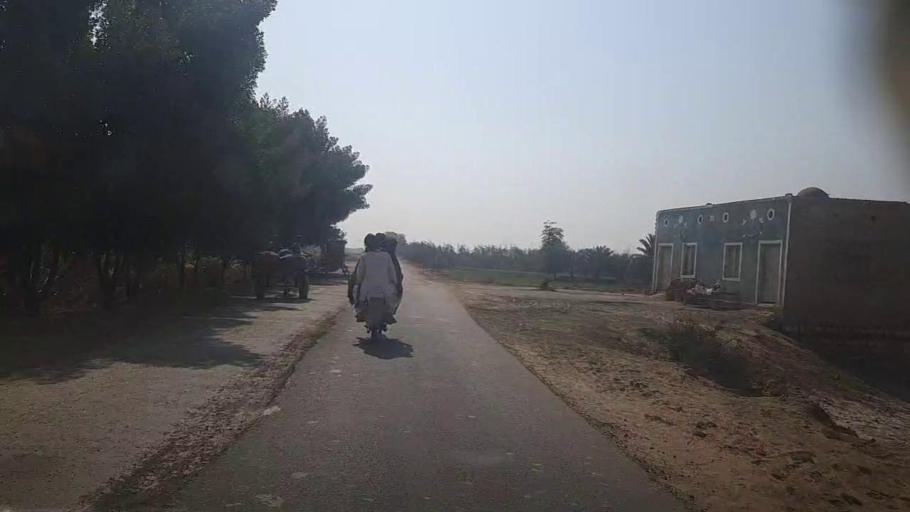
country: PK
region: Sindh
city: Khairpur
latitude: 27.4622
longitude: 68.8167
